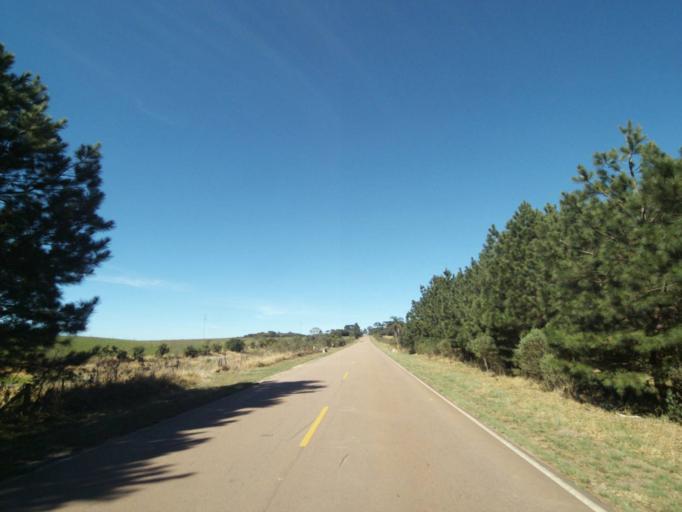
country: BR
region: Parana
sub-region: Tibagi
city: Tibagi
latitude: -24.6530
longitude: -50.2280
